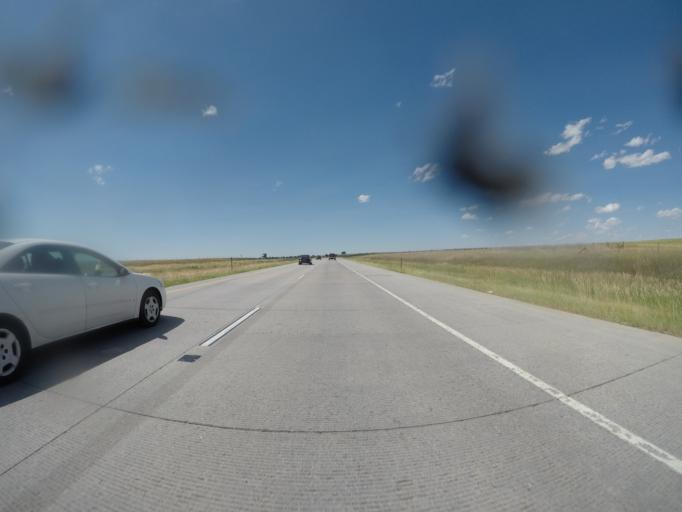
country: US
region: Colorado
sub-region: Arapahoe County
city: Byers
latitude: 39.5984
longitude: -104.0338
